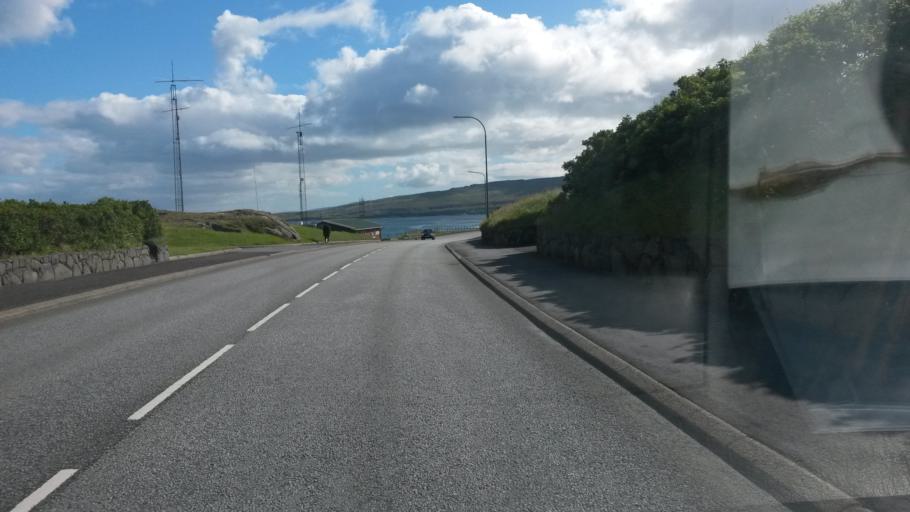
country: FO
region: Streymoy
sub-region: Torshavn
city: Torshavn
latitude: 62.0166
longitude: -6.7555
